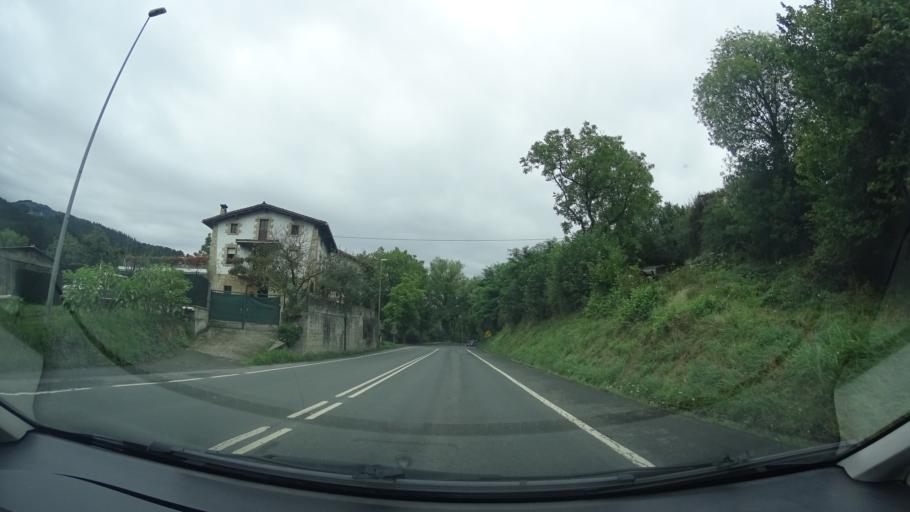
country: ES
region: Basque Country
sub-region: Bizkaia
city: Amorebieta
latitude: 43.1932
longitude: -2.7755
